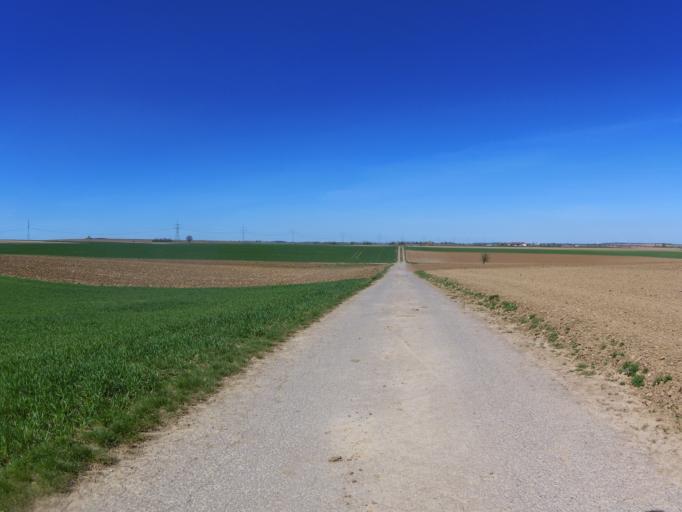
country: DE
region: Bavaria
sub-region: Regierungsbezirk Unterfranken
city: Biebelried
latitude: 49.8042
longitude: 10.0950
